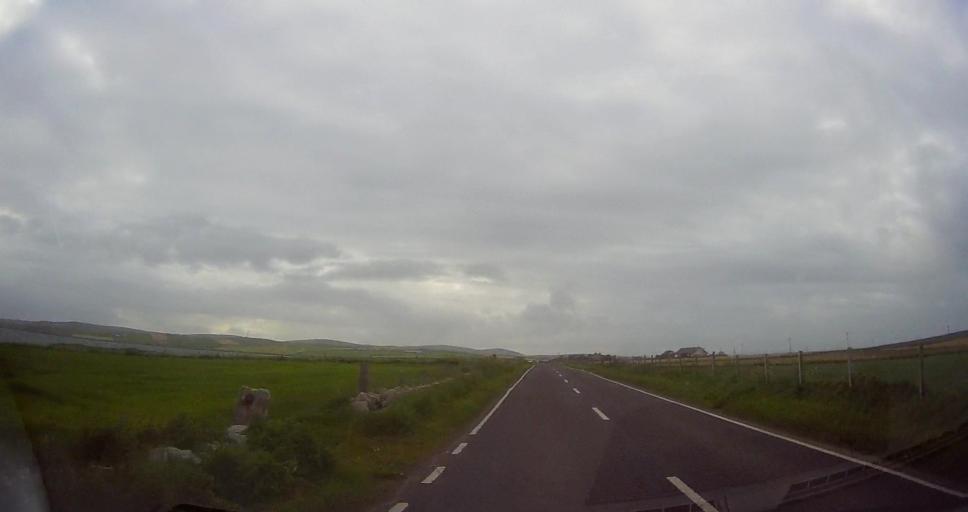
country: GB
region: Scotland
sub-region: Orkney Islands
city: Stromness
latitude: 58.9700
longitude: -3.2314
